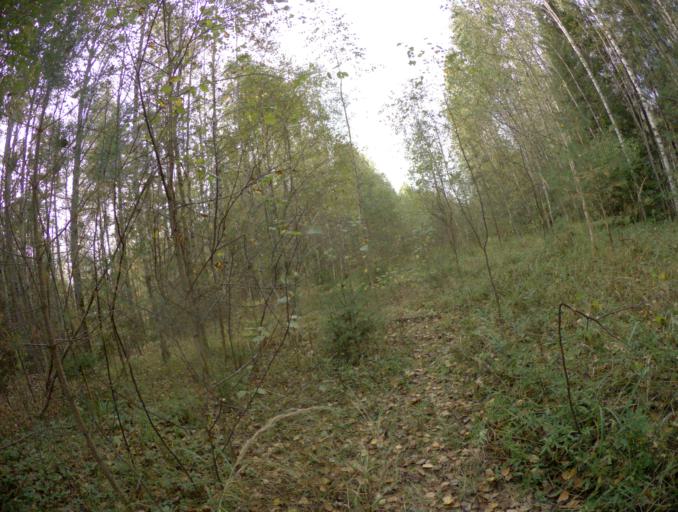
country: RU
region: Vladimir
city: Raduzhnyy
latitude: 55.9723
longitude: 40.2659
